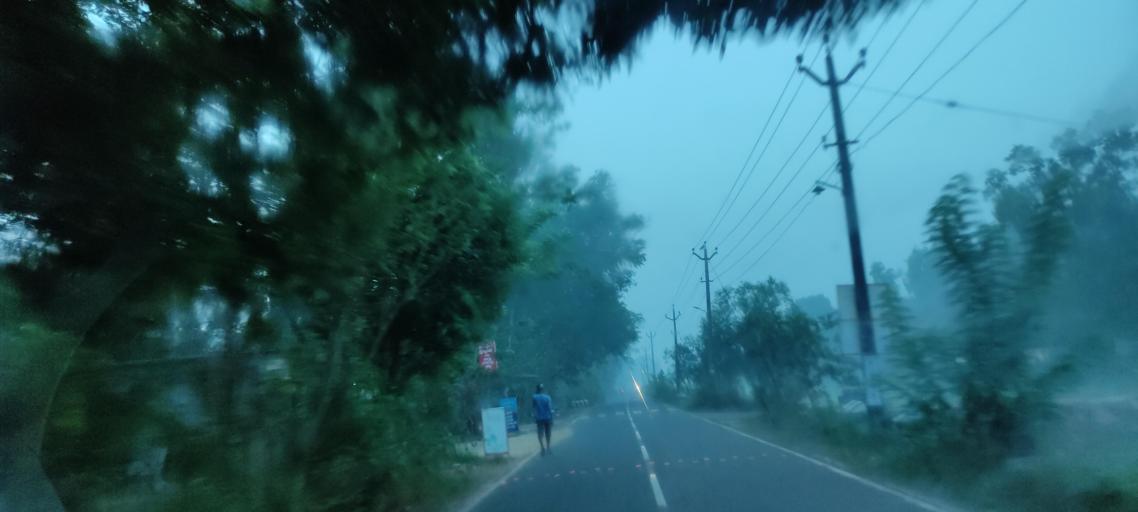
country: IN
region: Kerala
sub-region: Alappuzha
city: Alleppey
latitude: 9.5867
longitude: 76.3326
